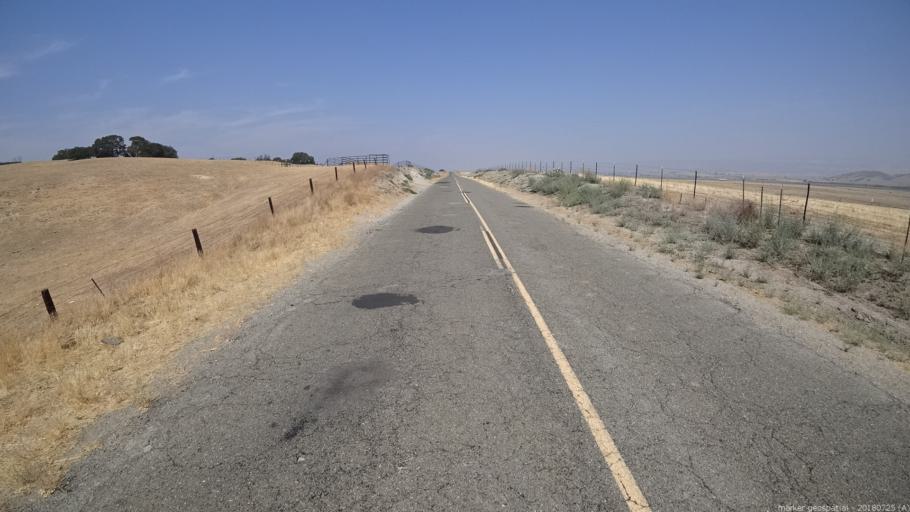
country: US
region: California
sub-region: San Luis Obispo County
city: Shandon
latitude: 35.8039
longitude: -120.3662
